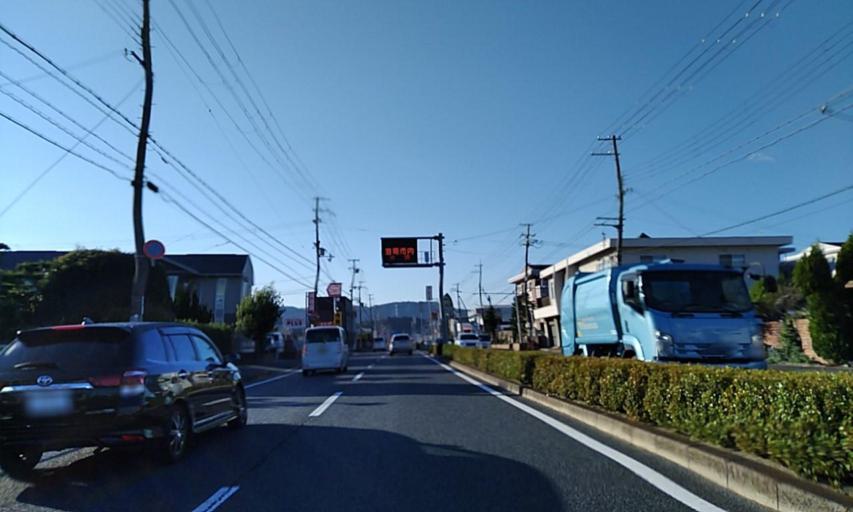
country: JP
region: Wakayama
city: Kainan
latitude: 34.1768
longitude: 135.1865
